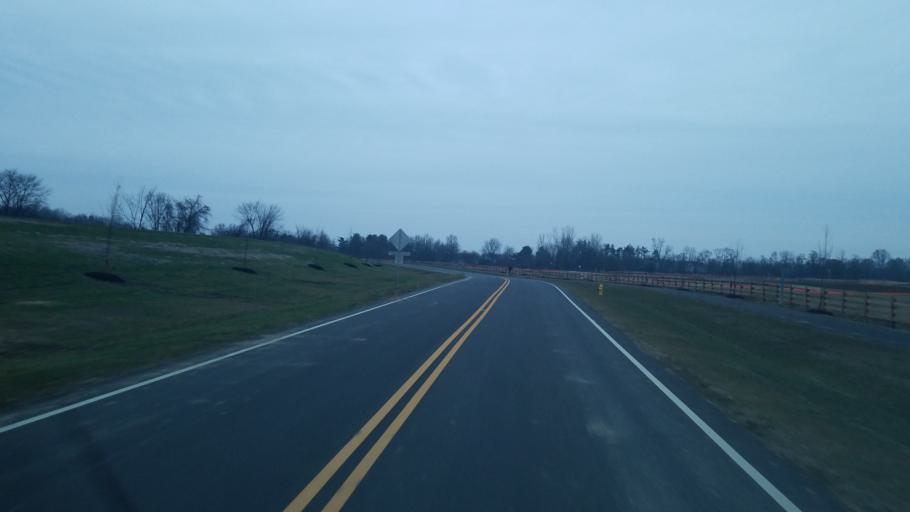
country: US
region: Ohio
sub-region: Delaware County
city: Sunbury
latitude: 40.2747
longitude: -82.9359
